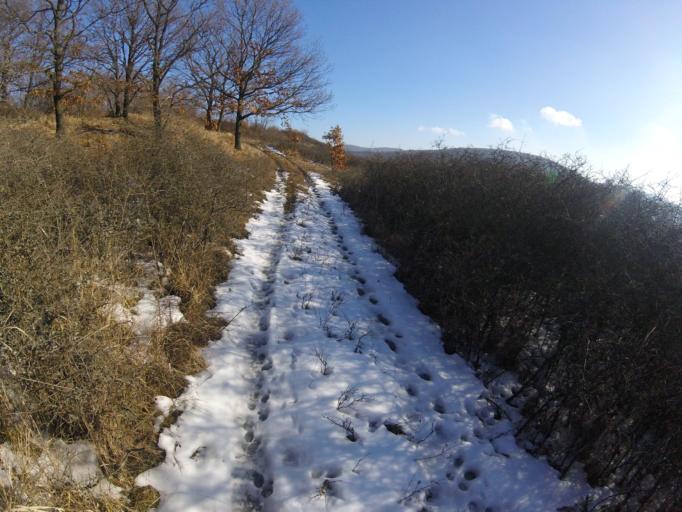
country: HU
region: Nograd
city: Rimoc
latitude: 48.0044
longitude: 19.5206
